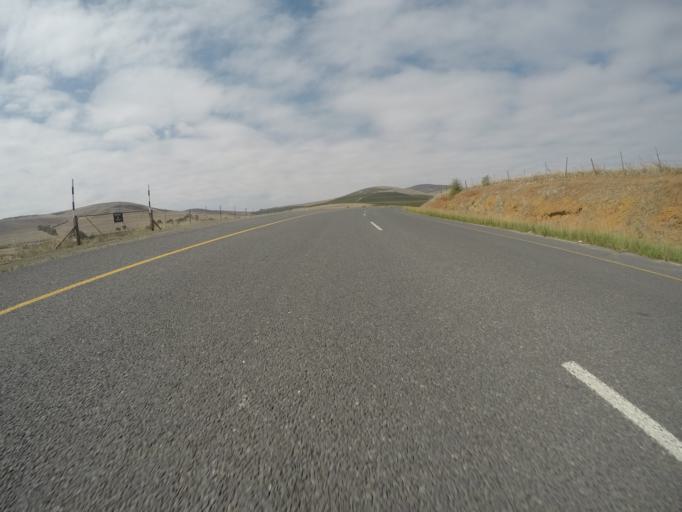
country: ZA
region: Western Cape
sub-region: City of Cape Town
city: Sunset Beach
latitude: -33.7881
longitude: 18.5792
